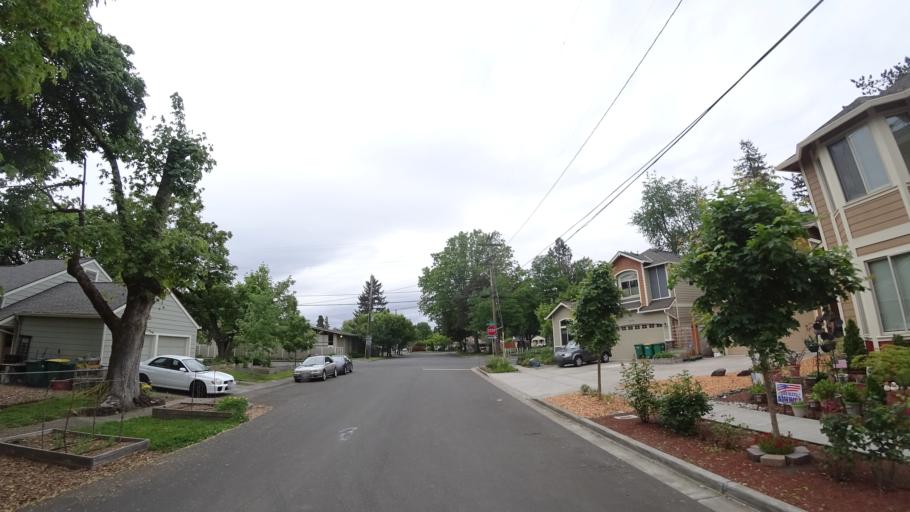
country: US
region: Oregon
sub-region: Washington County
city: Beaverton
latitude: 45.4822
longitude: -122.8077
